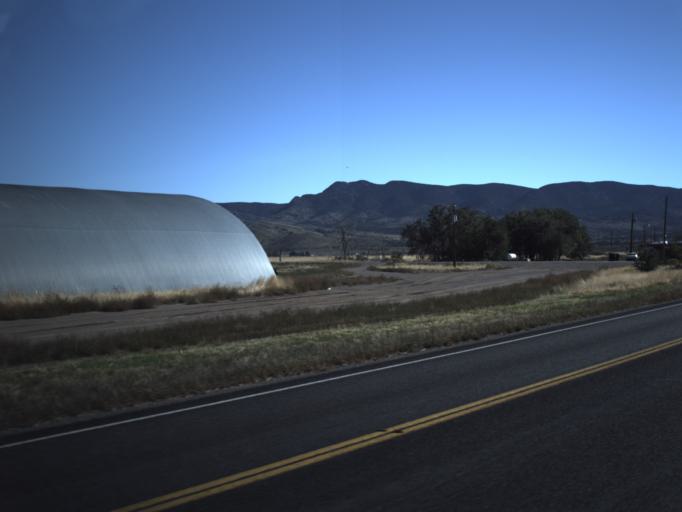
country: US
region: Utah
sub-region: Washington County
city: Enterprise
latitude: 37.6722
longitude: -113.5506
